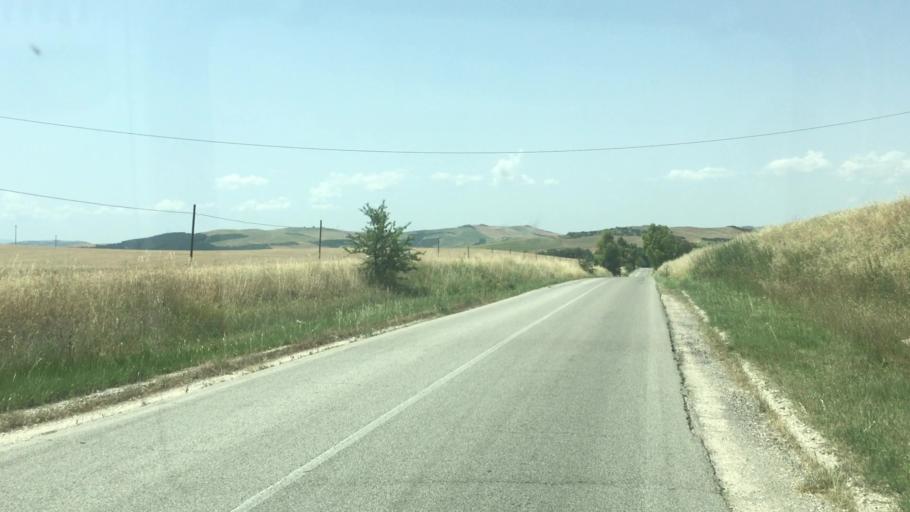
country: IT
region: Basilicate
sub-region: Provincia di Matera
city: La Martella
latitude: 40.6679
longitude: 16.4872
